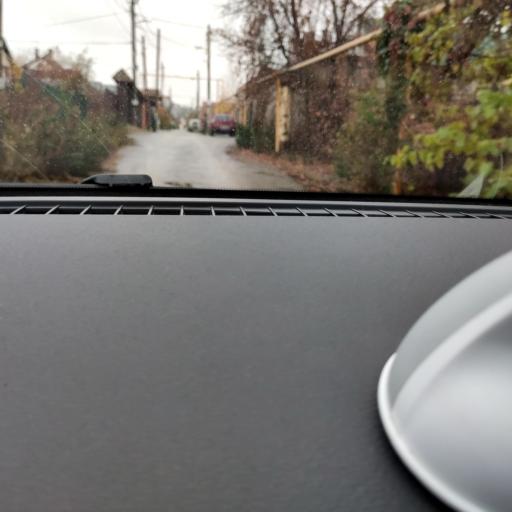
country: RU
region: Samara
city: Samara
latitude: 53.2719
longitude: 50.2095
